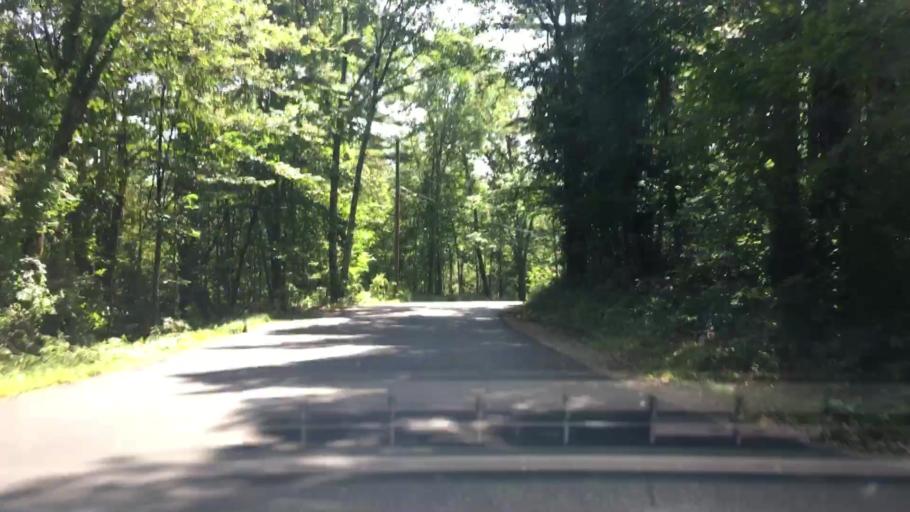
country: US
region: New Hampshire
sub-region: Rockingham County
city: Hampstead
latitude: 42.8836
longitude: -71.2210
